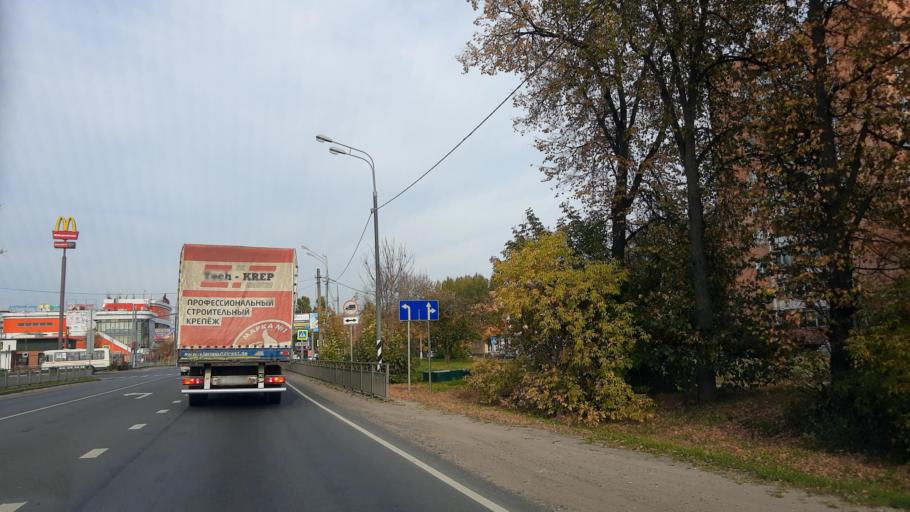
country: RU
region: Moskovskaya
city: Elektrostal'
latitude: 55.7685
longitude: 38.4350
